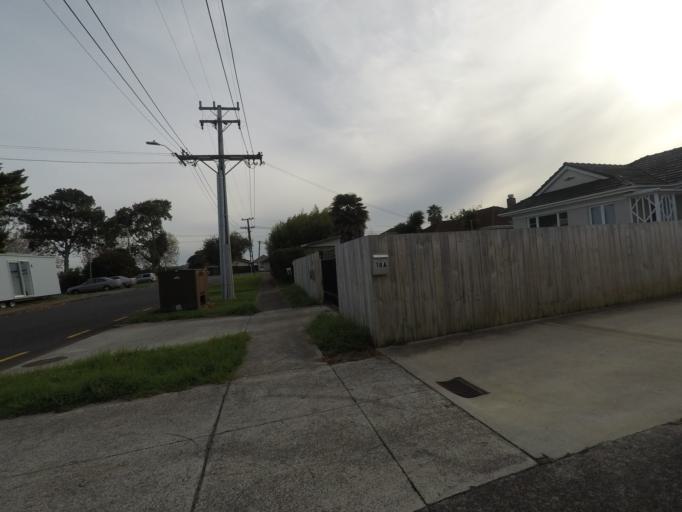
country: NZ
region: Auckland
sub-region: Auckland
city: Mangere
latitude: -36.9465
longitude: 174.8126
